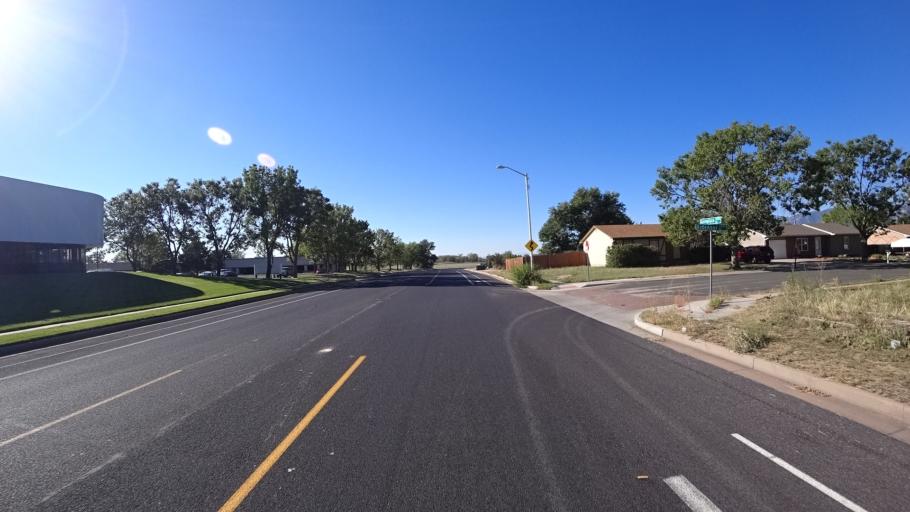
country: US
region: Colorado
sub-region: El Paso County
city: Cimarron Hills
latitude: 38.8144
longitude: -104.7325
